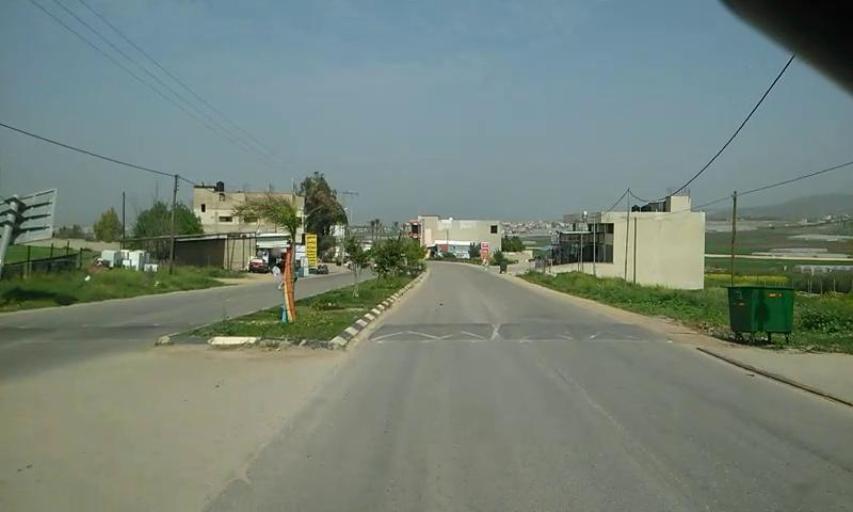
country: PS
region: West Bank
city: Al Jalamah
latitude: 32.4911
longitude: 35.3013
